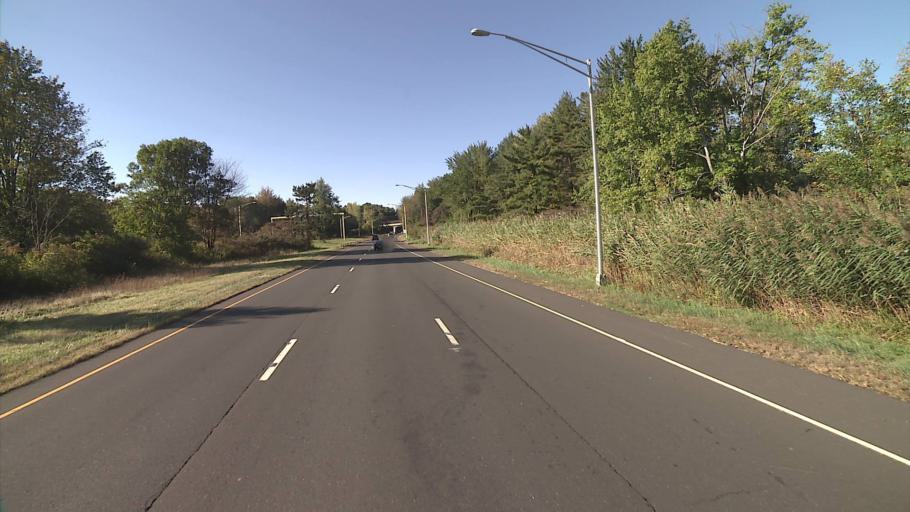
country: US
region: Connecticut
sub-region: New Haven County
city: Meriden
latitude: 41.5194
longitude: -72.7740
